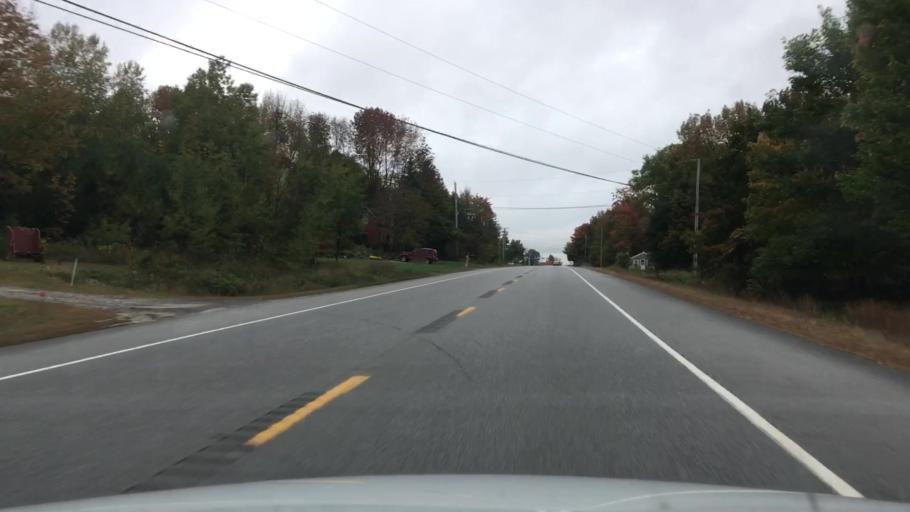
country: US
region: Maine
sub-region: Androscoggin County
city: Mechanic Falls
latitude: 44.1118
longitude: -70.4401
